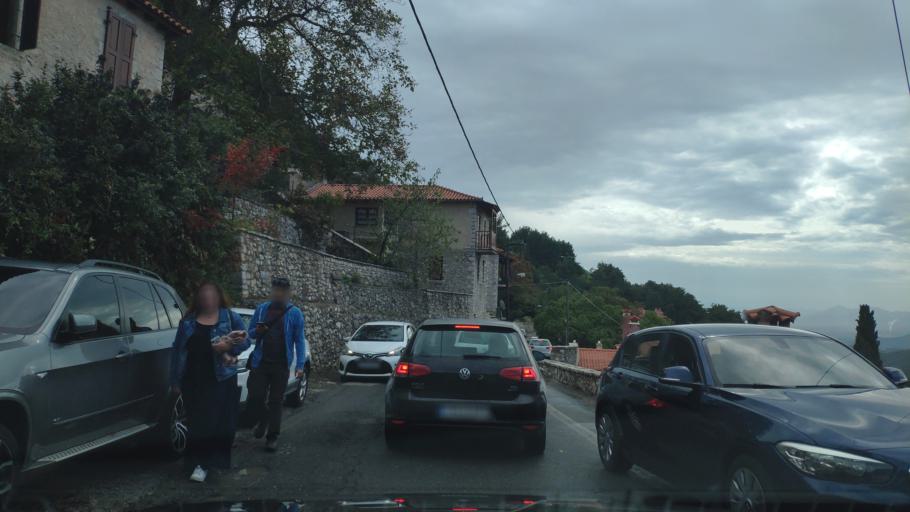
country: GR
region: Peloponnese
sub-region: Nomos Arkadias
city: Dimitsana
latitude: 37.5940
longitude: 22.0412
